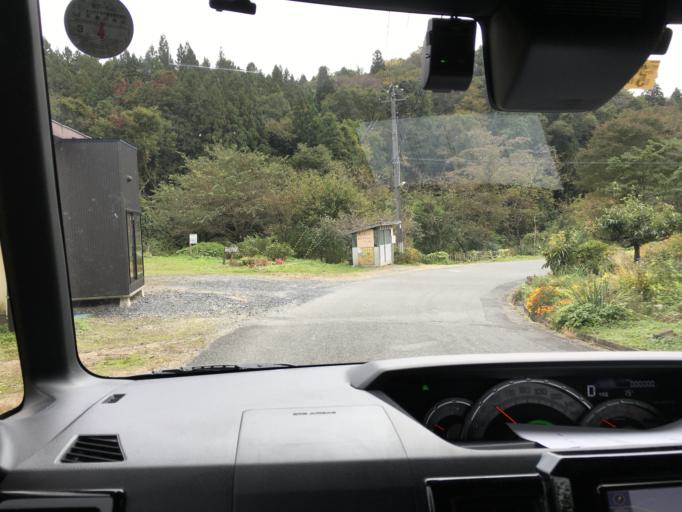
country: JP
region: Iwate
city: Ichinoseki
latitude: 39.0240
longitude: 141.3535
